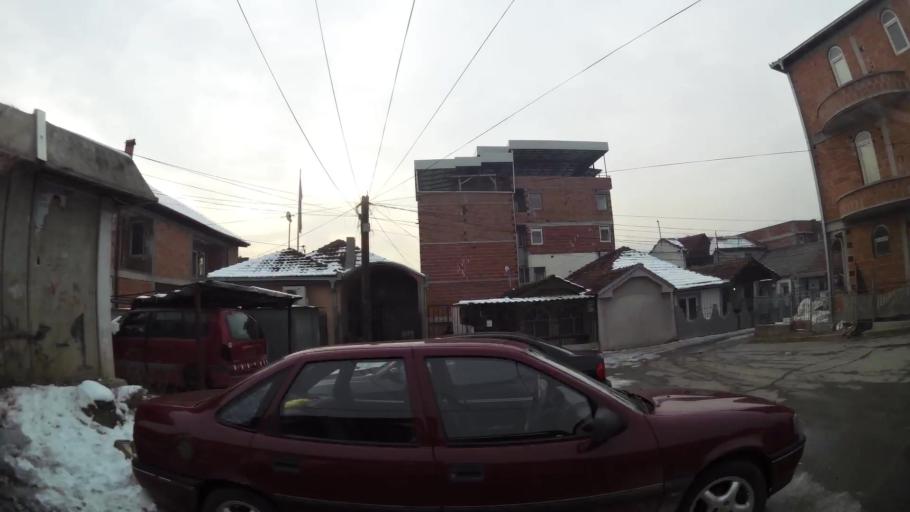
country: MK
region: Suto Orizari
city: Suto Orizare
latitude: 42.0419
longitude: 21.4245
